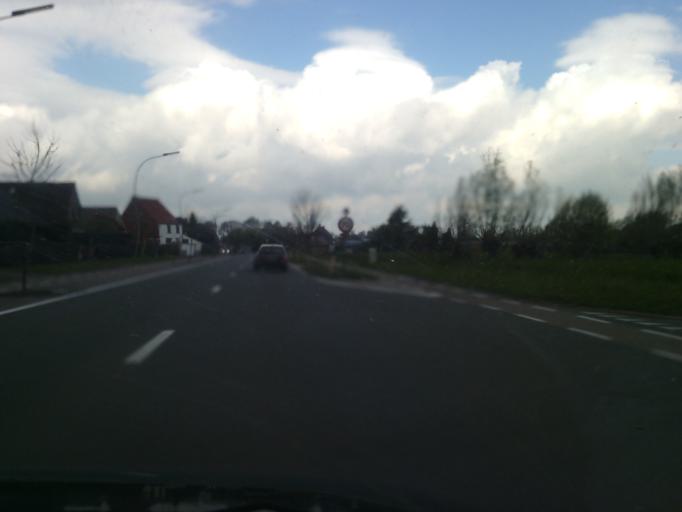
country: BE
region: Flanders
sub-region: Provincie Oost-Vlaanderen
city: Laarne
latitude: 51.0592
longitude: 3.8356
